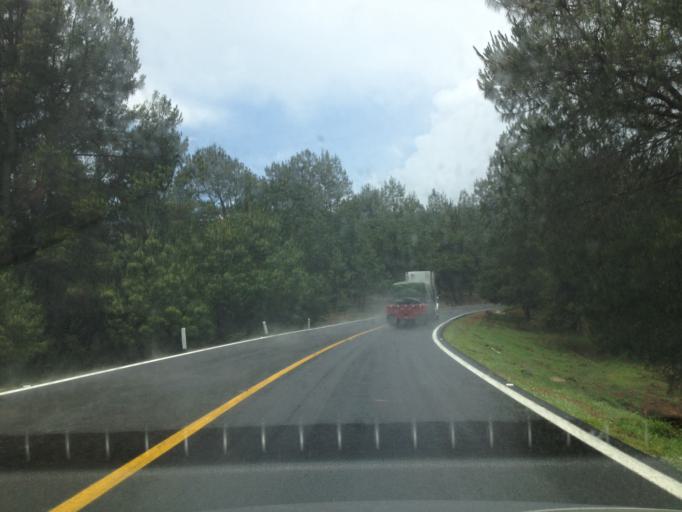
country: MX
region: Michoacan
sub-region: Patzcuaro
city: Santa Maria Huiramangaro (San Juan Tumbio)
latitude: 19.4910
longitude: -101.7815
